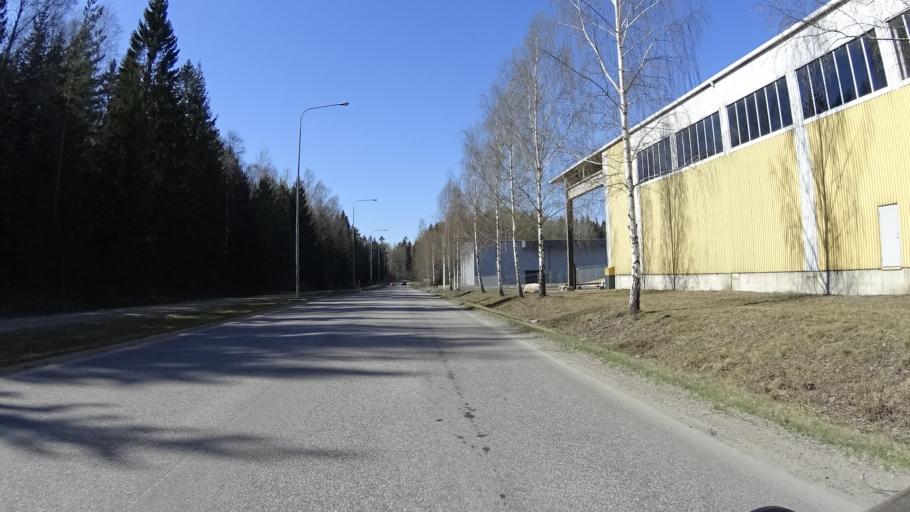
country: SE
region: Soedermanland
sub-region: Katrineholms Kommun
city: Katrineholm
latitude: 58.9926
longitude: 16.2381
